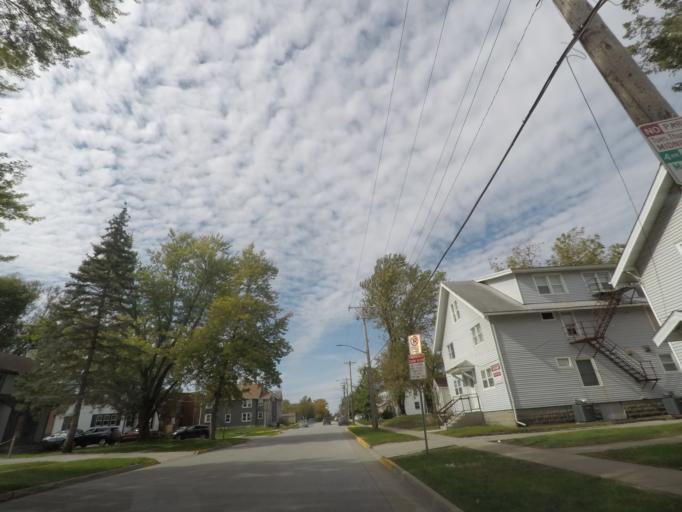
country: US
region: Iowa
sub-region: Story County
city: Ames
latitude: 42.0192
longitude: -93.6477
